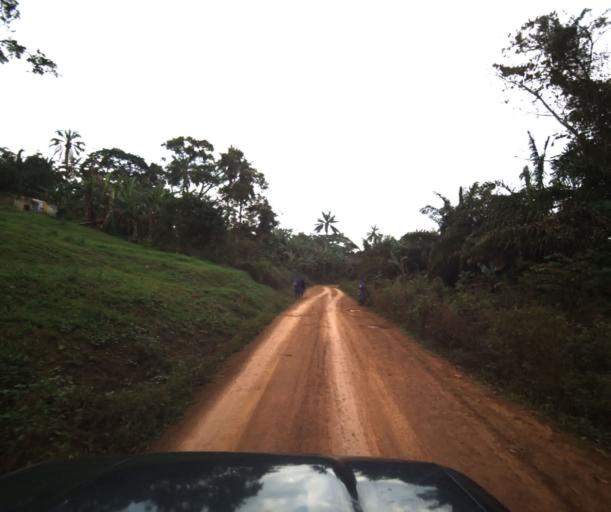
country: CM
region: Centre
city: Akono
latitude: 3.6057
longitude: 11.1902
